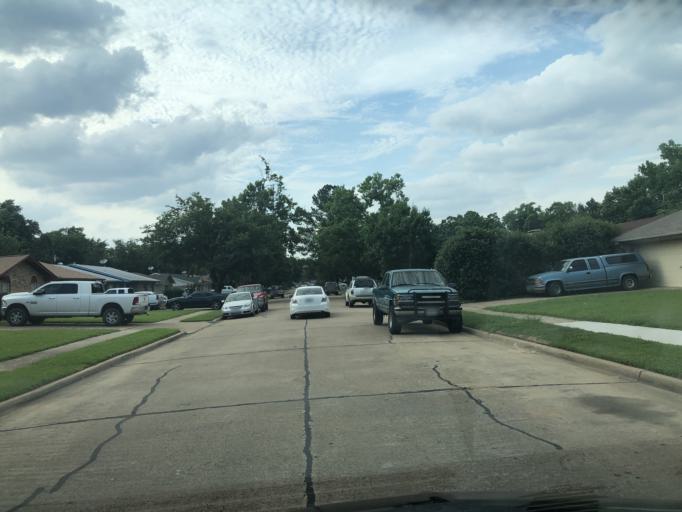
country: US
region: Texas
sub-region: Dallas County
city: Irving
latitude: 32.7900
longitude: -96.9727
